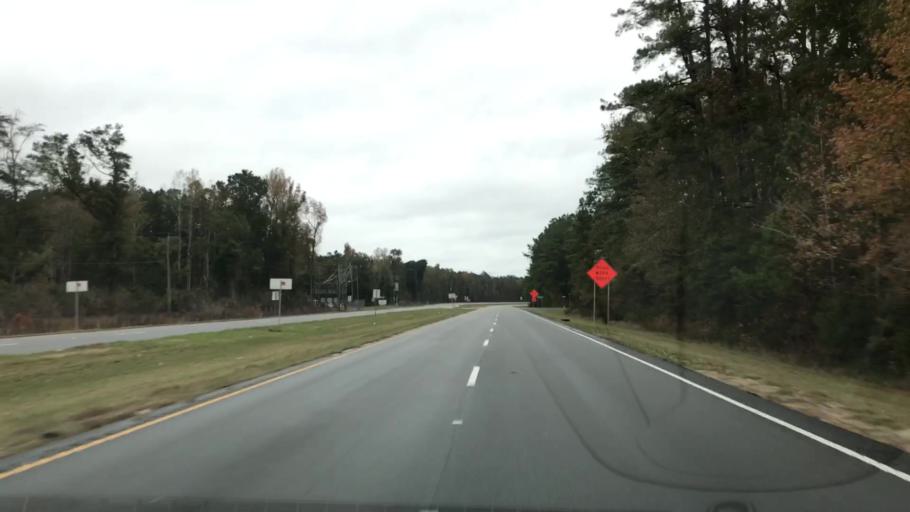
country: US
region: South Carolina
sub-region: Georgetown County
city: Georgetown
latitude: 33.2910
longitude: -79.3474
